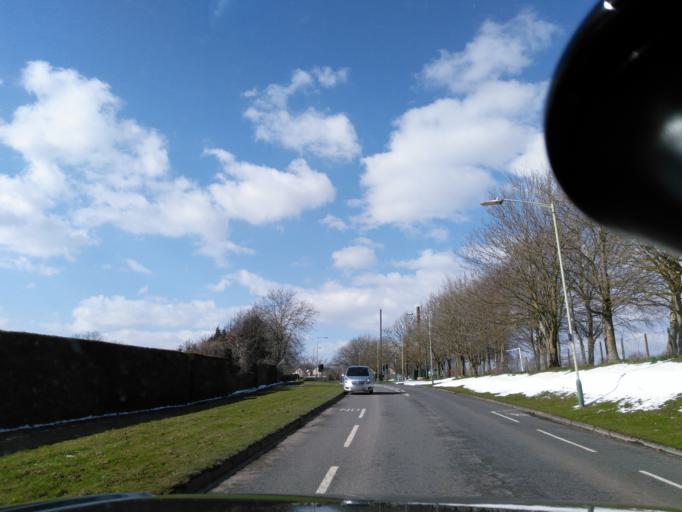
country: GB
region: England
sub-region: Wiltshire
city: Corsham
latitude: 51.4296
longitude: -2.1949
